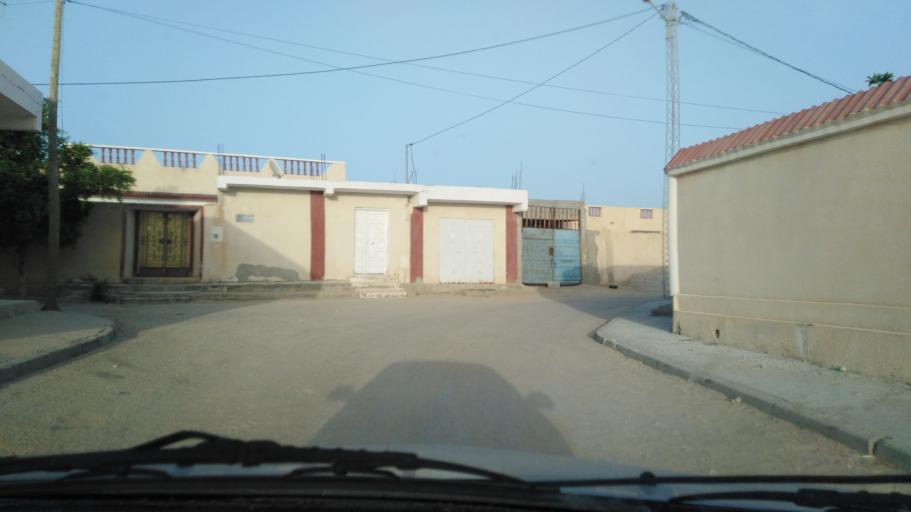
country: TN
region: Qabis
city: Gabes
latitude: 33.9547
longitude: 9.9953
